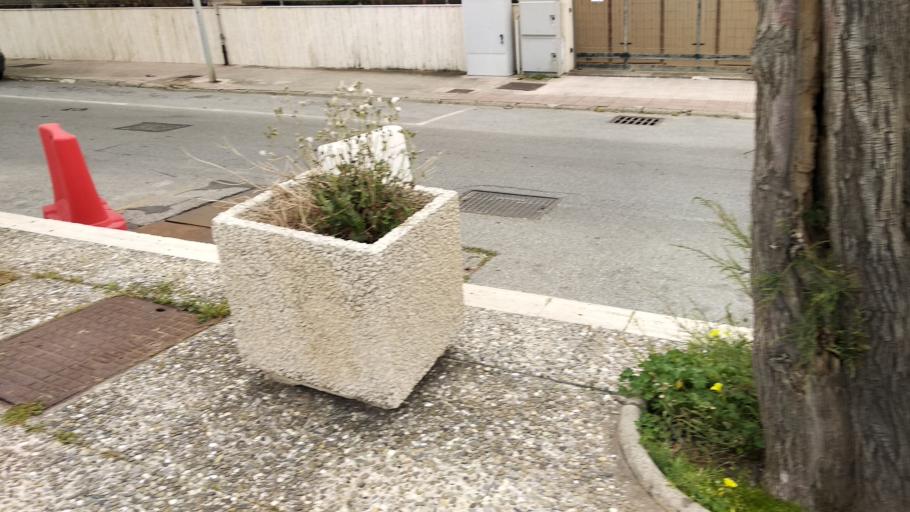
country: IT
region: Sicily
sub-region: Messina
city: Venetico Marina
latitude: 38.2210
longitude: 15.3667
